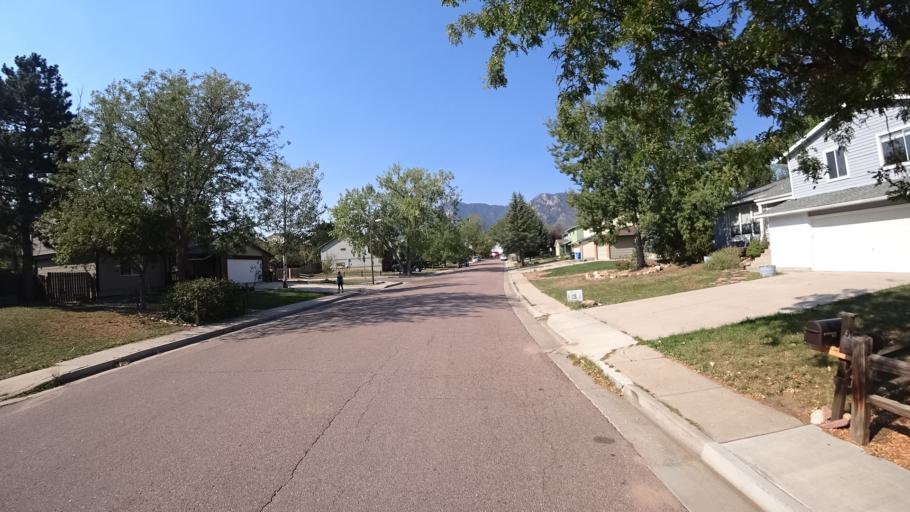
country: US
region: Colorado
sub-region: El Paso County
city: Stratmoor
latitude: 38.7830
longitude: -104.8145
